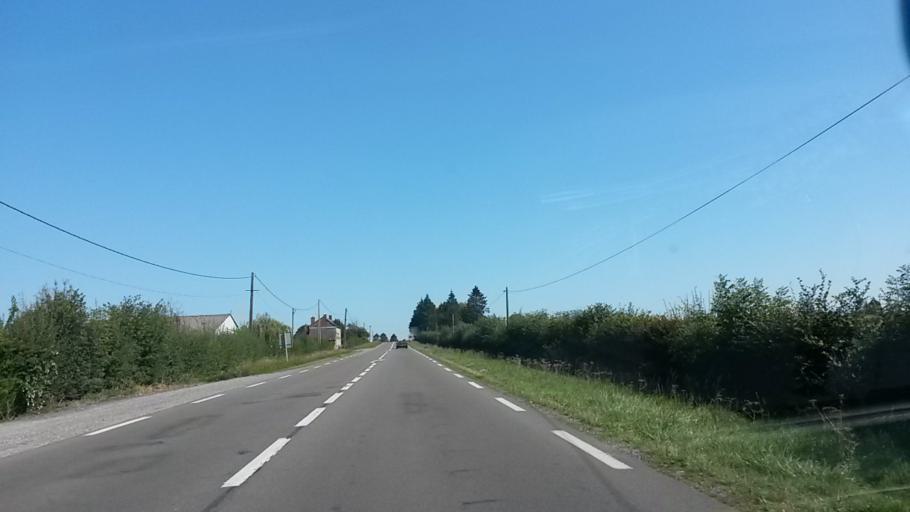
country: FR
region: Nord-Pas-de-Calais
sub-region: Departement du Nord
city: Avesnelles
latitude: 50.1498
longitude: 3.9516
